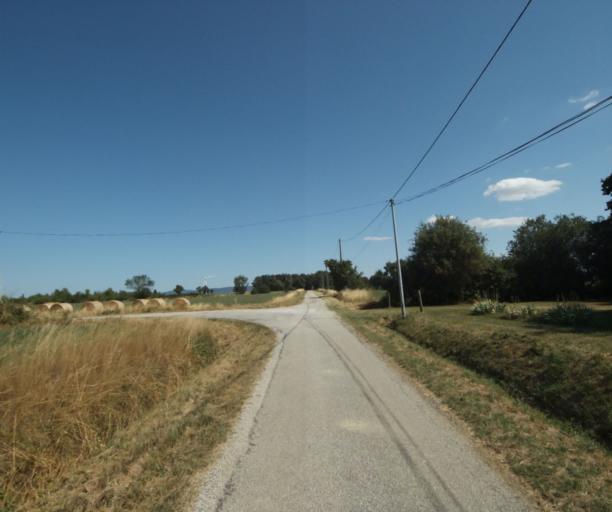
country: FR
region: Midi-Pyrenees
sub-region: Departement de la Haute-Garonne
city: Saint-Felix-Lauragais
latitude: 43.4756
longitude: 1.9036
